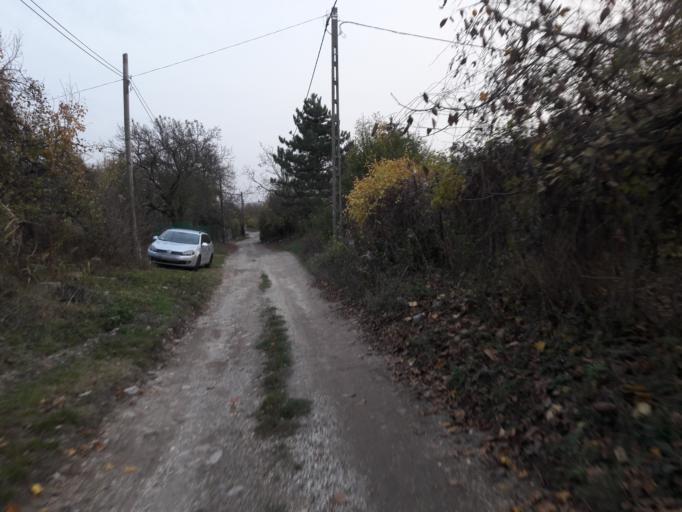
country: HU
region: Pest
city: Budaors
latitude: 47.4713
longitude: 18.9795
